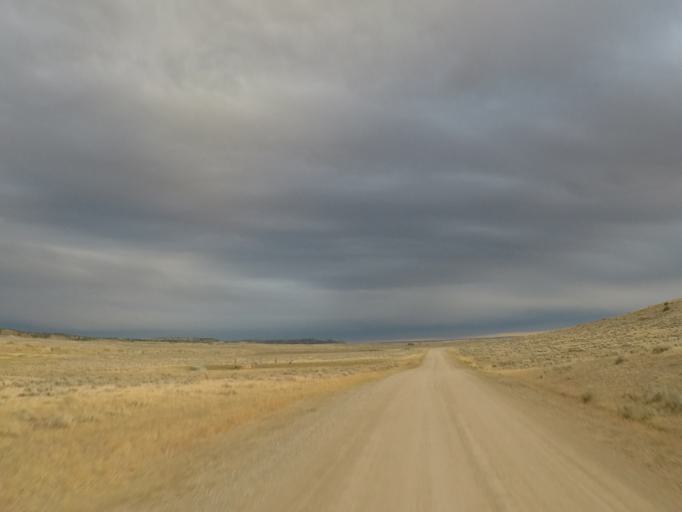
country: US
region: Montana
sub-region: Golden Valley County
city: Ryegate
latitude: 46.4308
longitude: -109.2525
